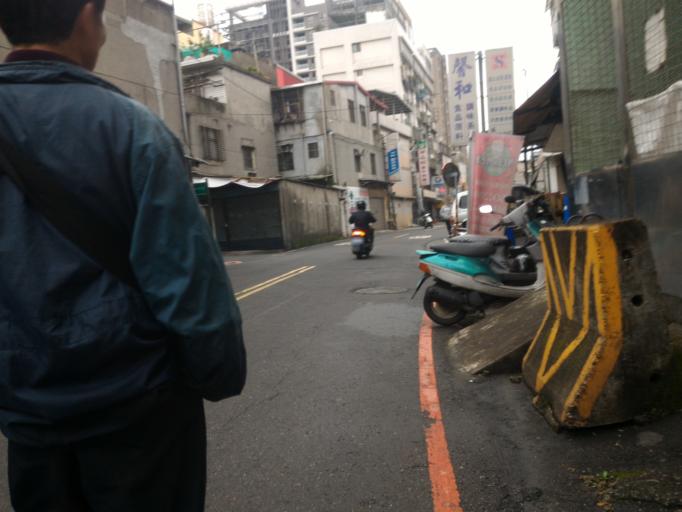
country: TW
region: Taipei
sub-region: Taipei
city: Banqiao
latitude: 25.0397
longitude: 121.4568
